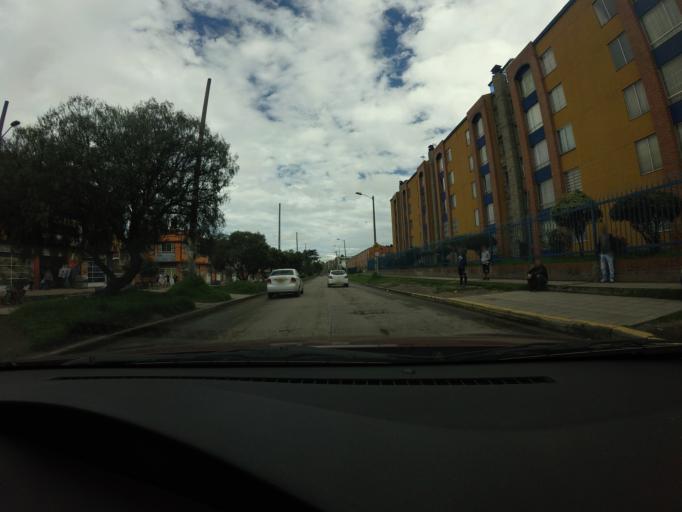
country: CO
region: Bogota D.C.
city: Bogota
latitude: 4.6028
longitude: -74.1493
